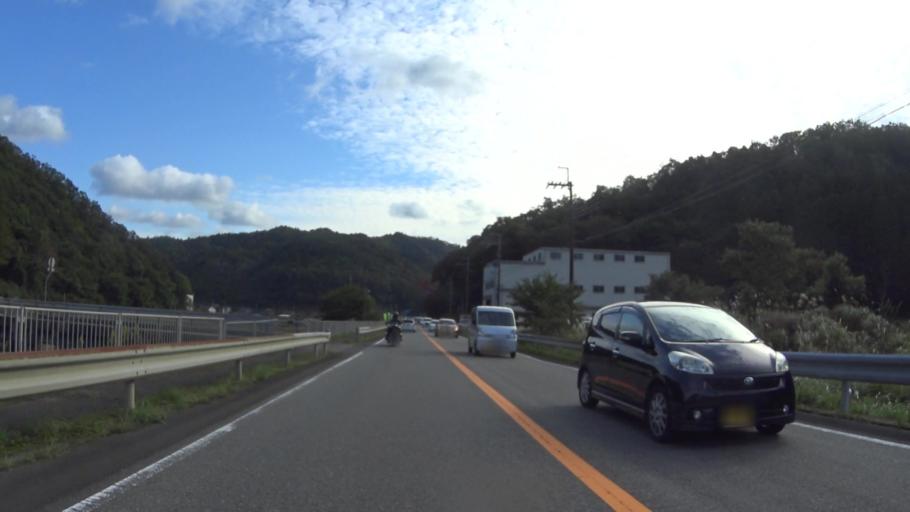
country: JP
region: Hyogo
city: Sasayama
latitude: 35.1217
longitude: 135.3365
